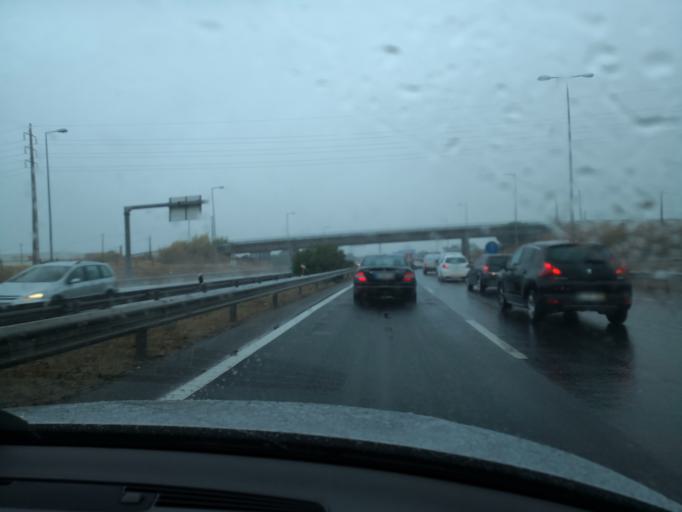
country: PT
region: Setubal
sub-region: Montijo
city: Montijo
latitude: 38.7027
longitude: -8.9406
